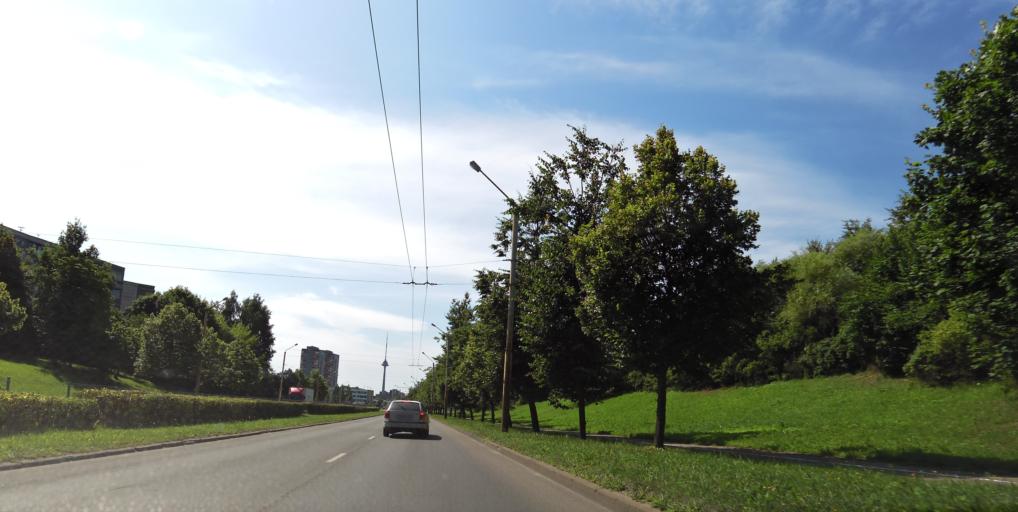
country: LT
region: Vilnius County
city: Justiniskes
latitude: 54.7084
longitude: 25.2156
